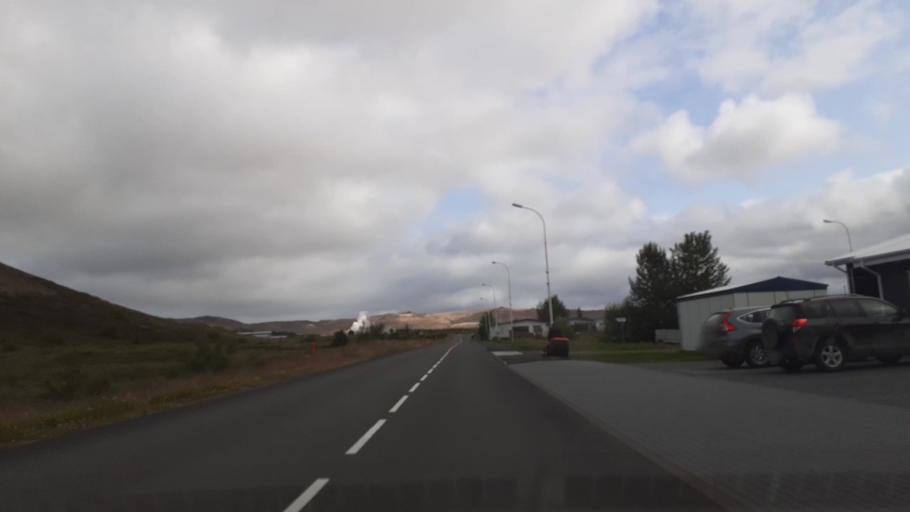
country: IS
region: Northeast
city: Laugar
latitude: 65.6423
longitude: -16.9062
